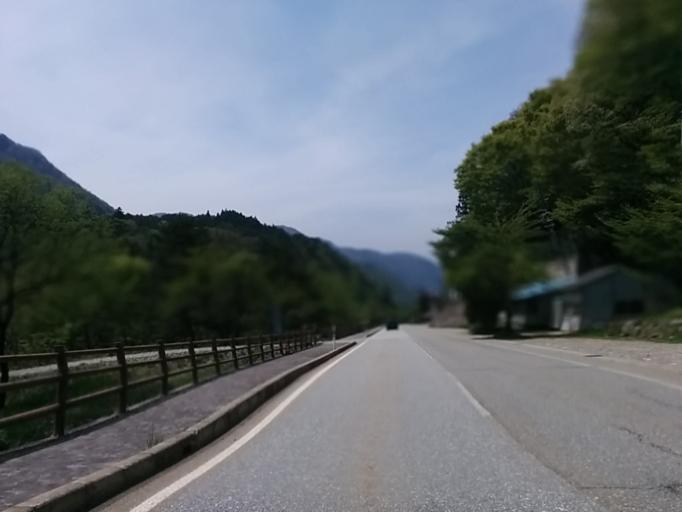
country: JP
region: Gifu
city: Takayama
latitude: 36.2455
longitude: 137.5278
